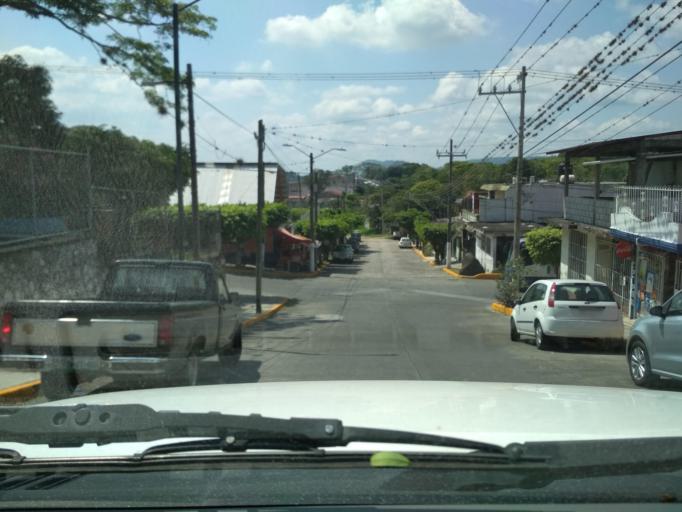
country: MX
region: Veracruz
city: Cordoba
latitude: 18.8772
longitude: -96.9138
